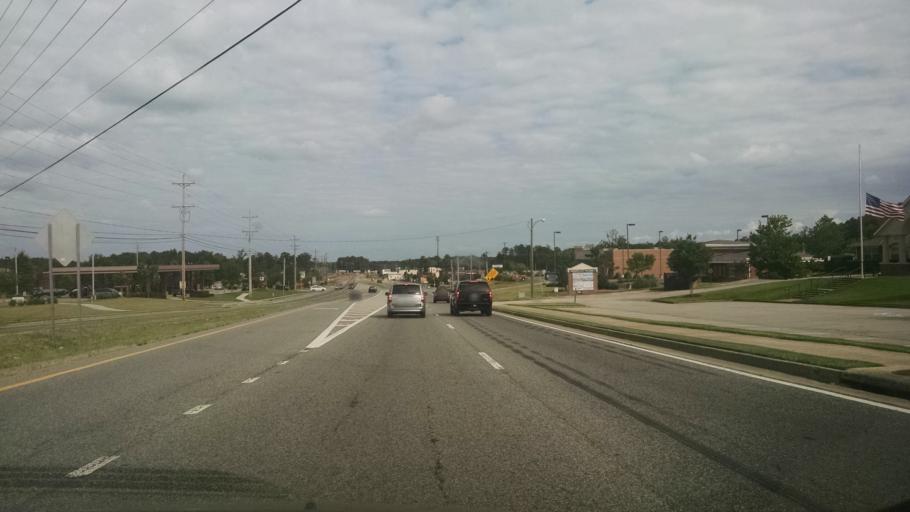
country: US
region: Georgia
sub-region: Forsyth County
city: Cumming
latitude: 34.1640
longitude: -84.1190
